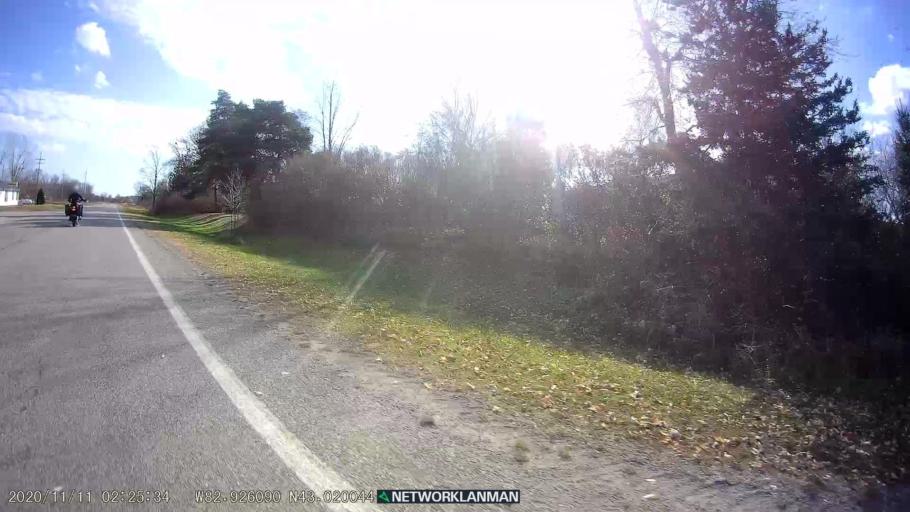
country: US
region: Michigan
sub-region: Saint Clair County
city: Capac
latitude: 43.0200
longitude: -82.9260
